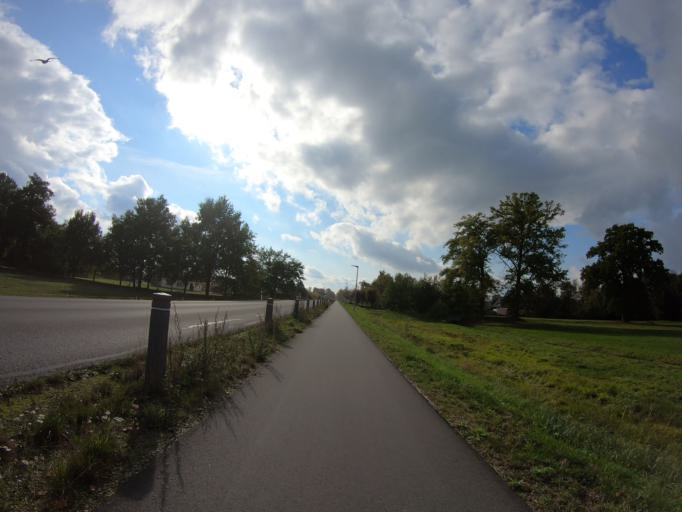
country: DE
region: Lower Saxony
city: Sassenburg
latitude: 52.5491
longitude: 10.6145
